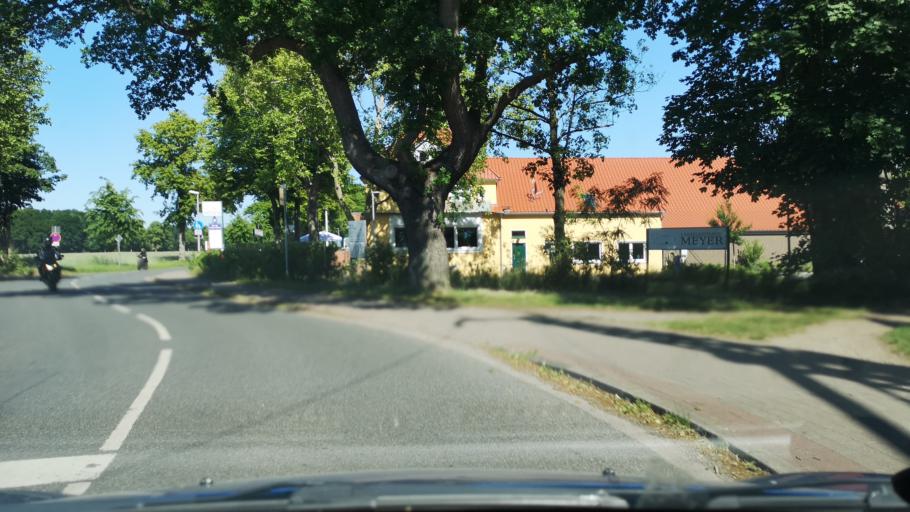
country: DE
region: Lower Saxony
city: Neustadt am Rubenberge
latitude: 52.4673
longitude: 9.4540
